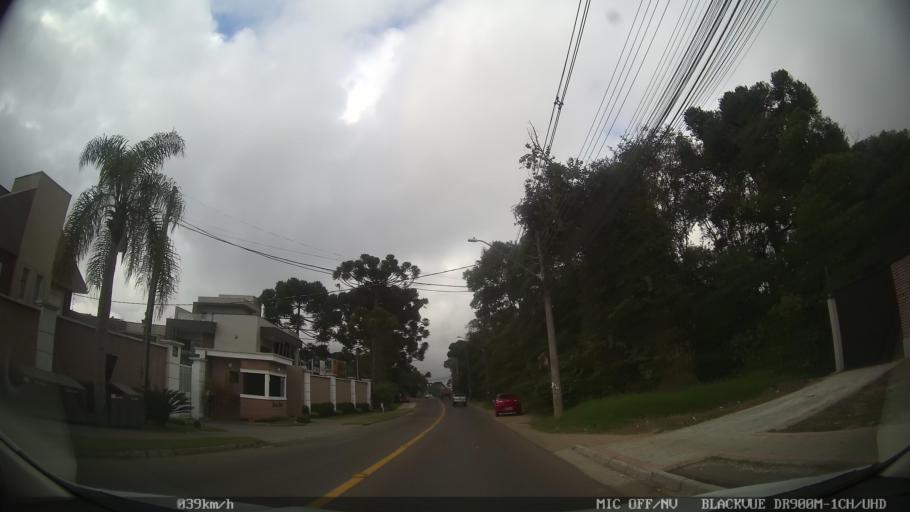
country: BR
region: Parana
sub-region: Curitiba
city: Curitiba
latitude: -25.3676
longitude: -49.2381
